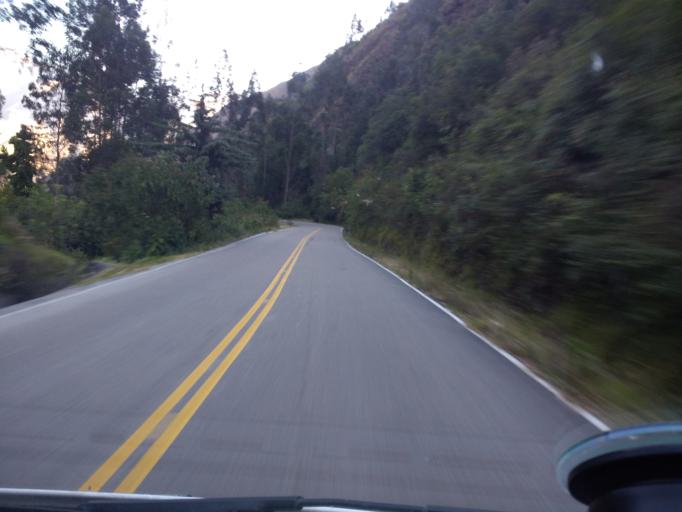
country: PE
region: Cusco
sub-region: Provincia de Urubamba
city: Ollantaytambo
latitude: -13.2011
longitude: -72.2960
